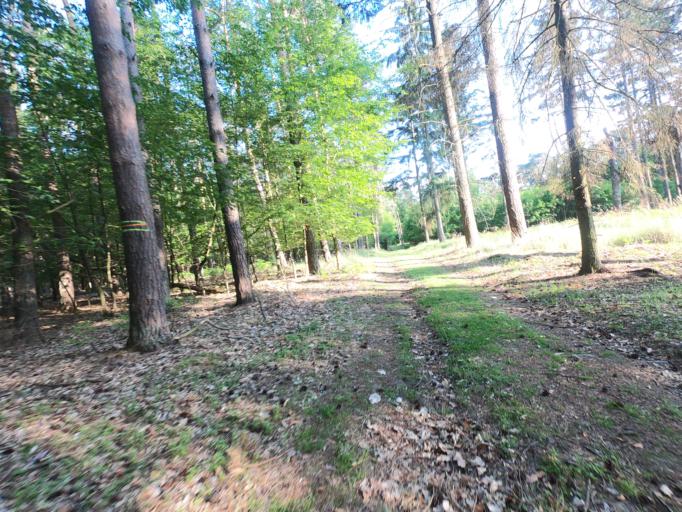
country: DE
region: Hesse
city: Kelsterbach
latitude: 50.0214
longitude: 8.5342
